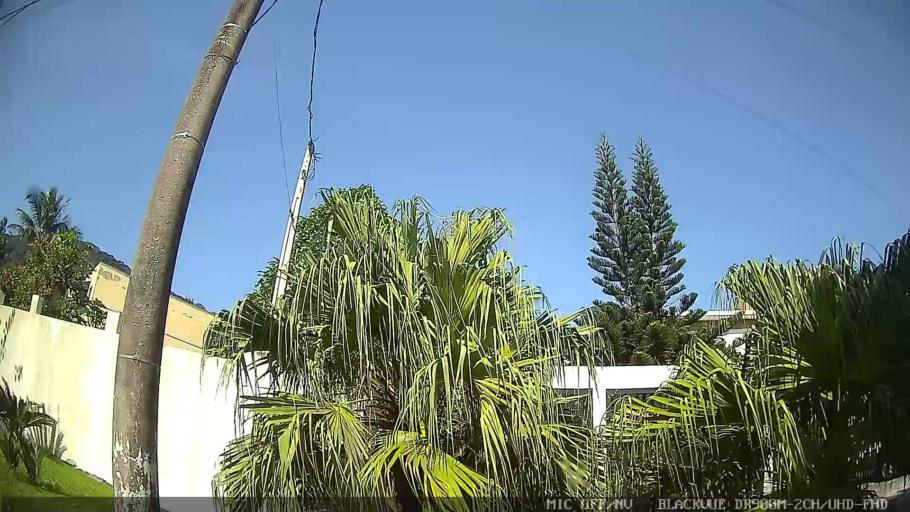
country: BR
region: Sao Paulo
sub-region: Guaruja
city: Guaruja
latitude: -24.0173
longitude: -46.2901
